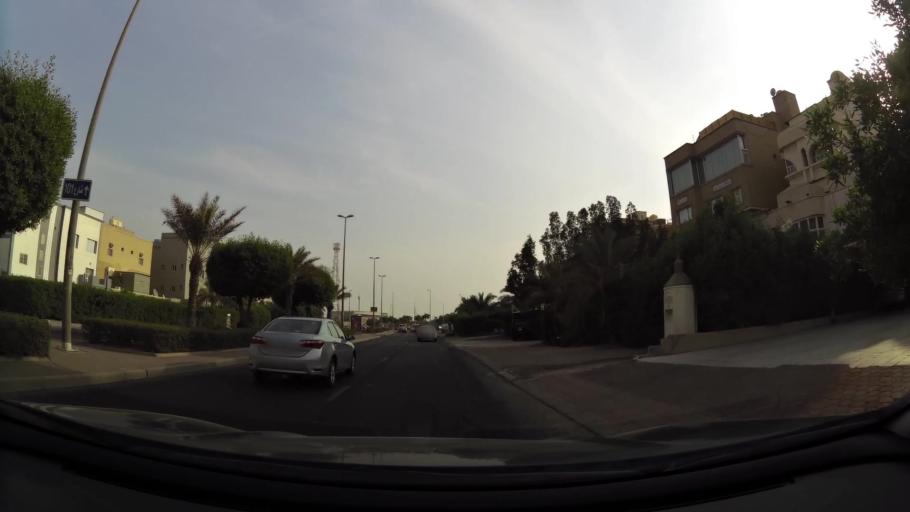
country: KW
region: Mubarak al Kabir
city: Sabah as Salim
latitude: 29.2389
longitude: 48.0615
